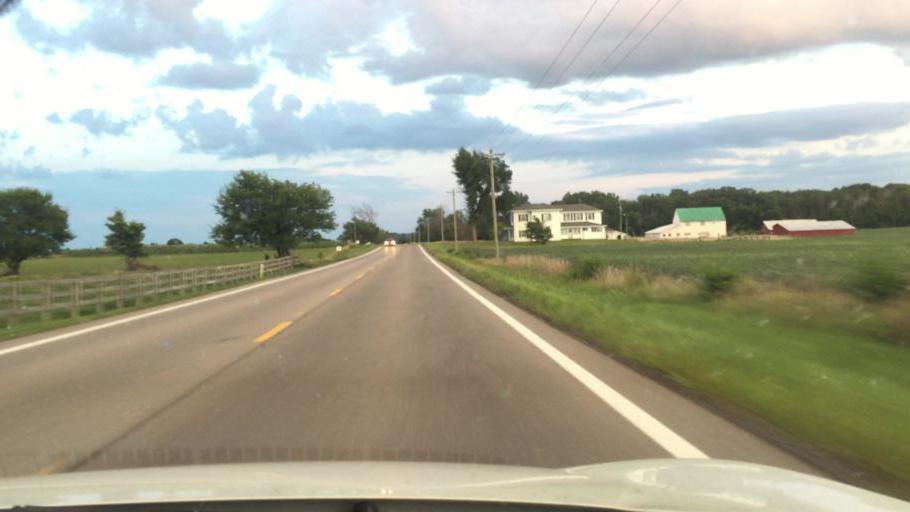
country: US
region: Ohio
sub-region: Champaign County
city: Mechanicsburg
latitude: 40.0535
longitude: -83.5281
